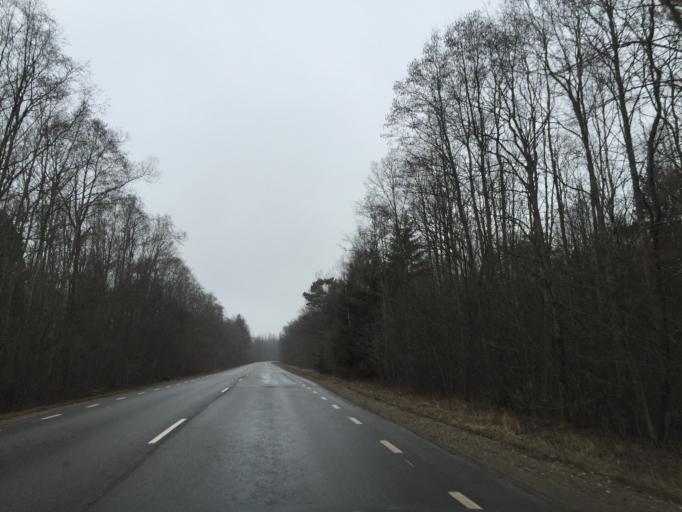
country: EE
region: Laeaene
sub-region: Lihula vald
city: Lihula
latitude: 58.6044
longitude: 23.6979
